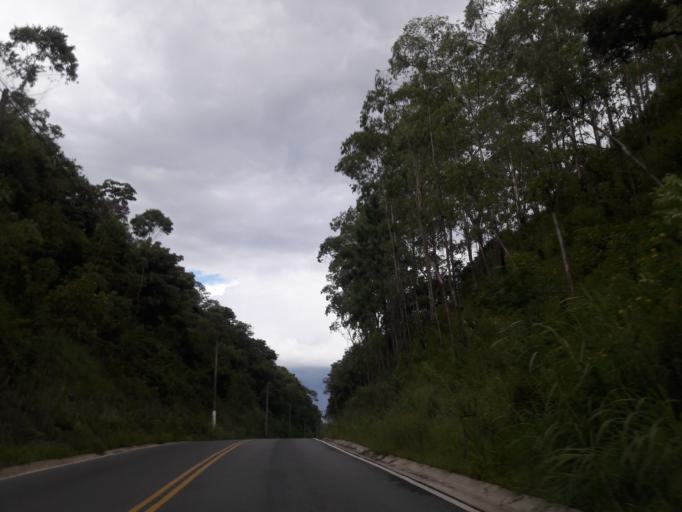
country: BR
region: Sao Paulo
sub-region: Aruja
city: Aruja
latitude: -23.3764
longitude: -46.4188
